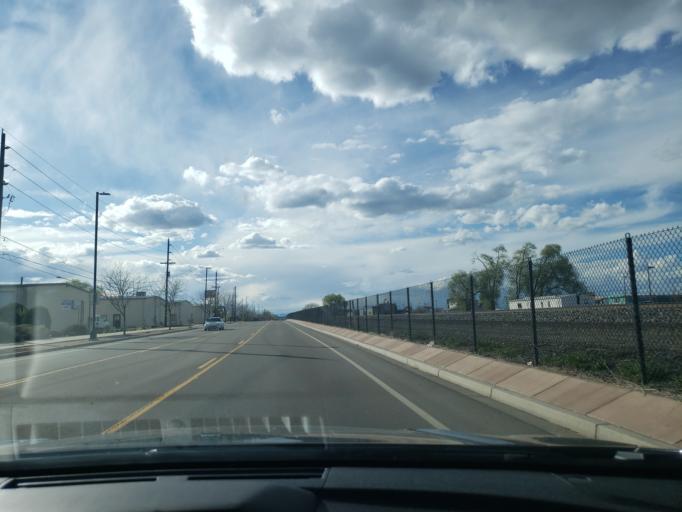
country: US
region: Colorado
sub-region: Mesa County
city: Redlands
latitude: 39.0823
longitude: -108.5921
